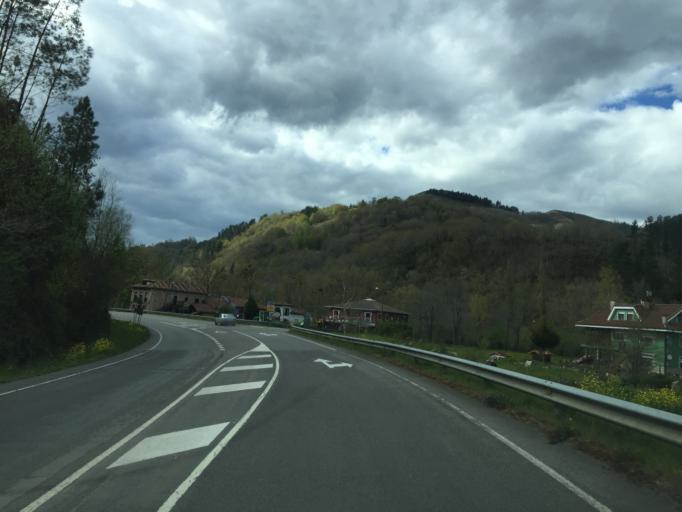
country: ES
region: Asturias
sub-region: Province of Asturias
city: Cangas de Onis
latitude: 43.3505
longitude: -5.0945
